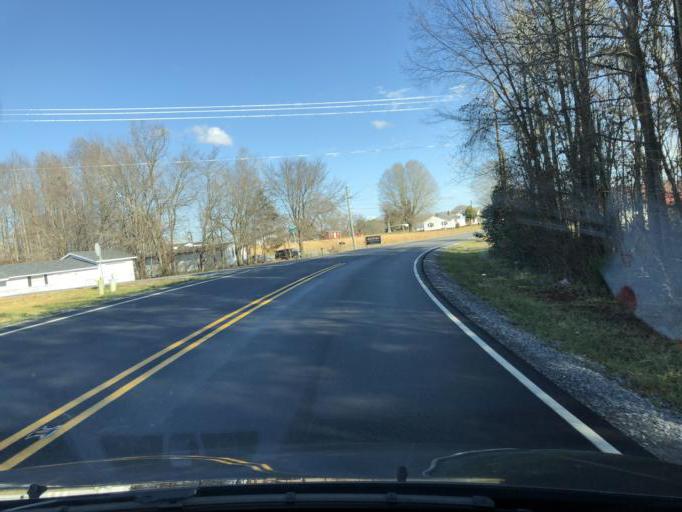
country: US
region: North Carolina
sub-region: Cleveland County
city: Shelby
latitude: 35.2059
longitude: -81.5567
